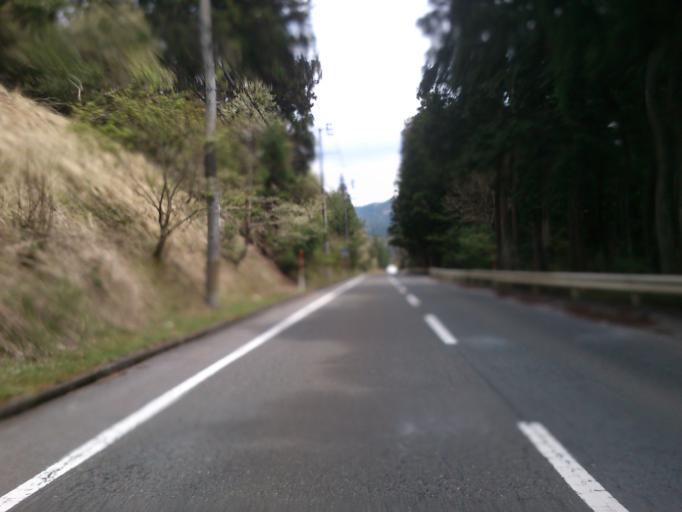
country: JP
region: Kyoto
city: Kameoka
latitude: 35.1997
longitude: 135.6266
